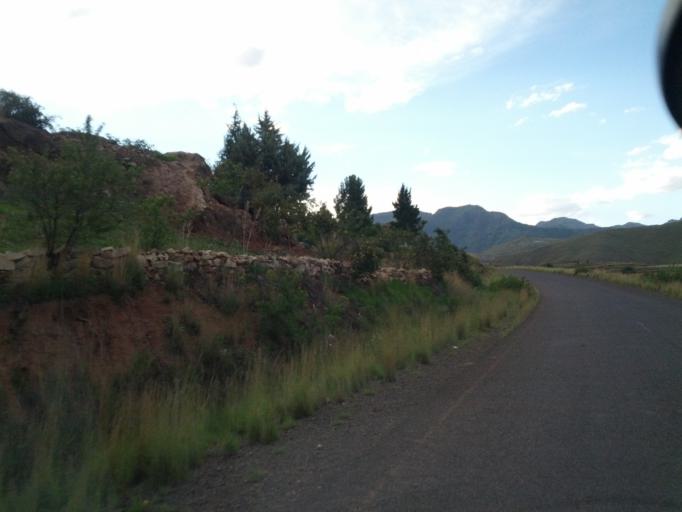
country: LS
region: Qacha's Nek
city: Qacha's Nek
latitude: -30.0673
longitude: 28.5331
